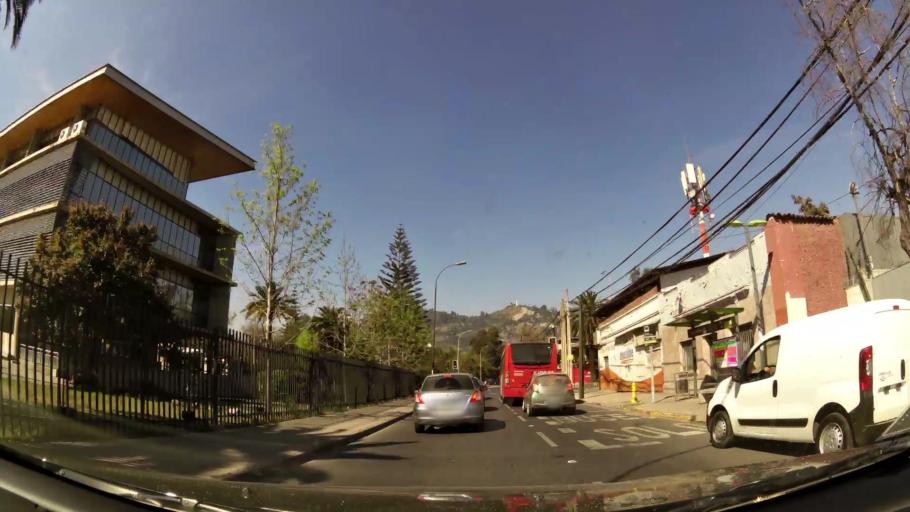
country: CL
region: Santiago Metropolitan
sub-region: Provincia de Santiago
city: Santiago
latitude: -33.4233
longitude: -70.6515
